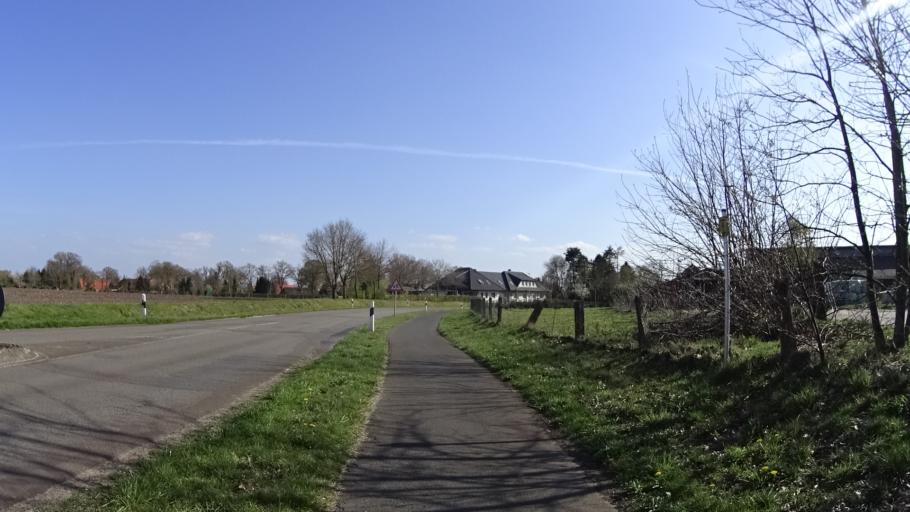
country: DE
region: Lower Saxony
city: Kluse
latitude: 52.9412
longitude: 7.3178
